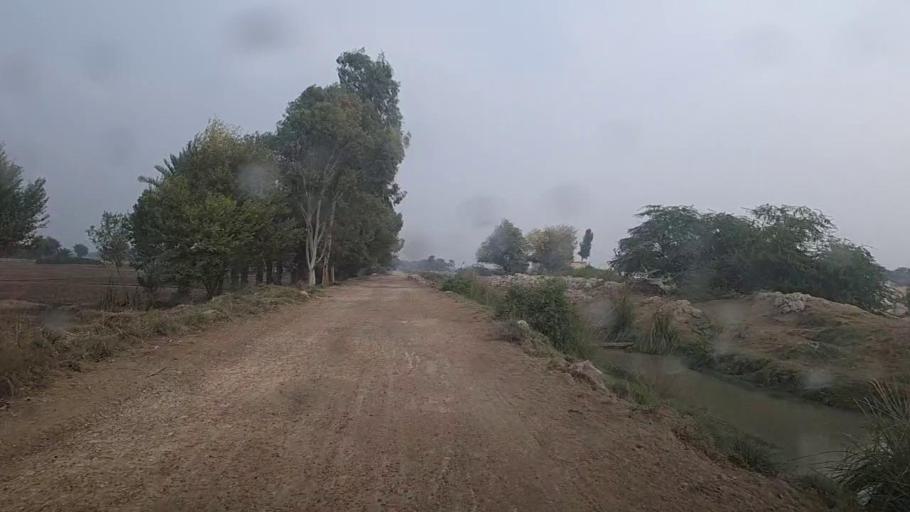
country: PK
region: Sindh
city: Gambat
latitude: 27.3847
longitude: 68.5869
